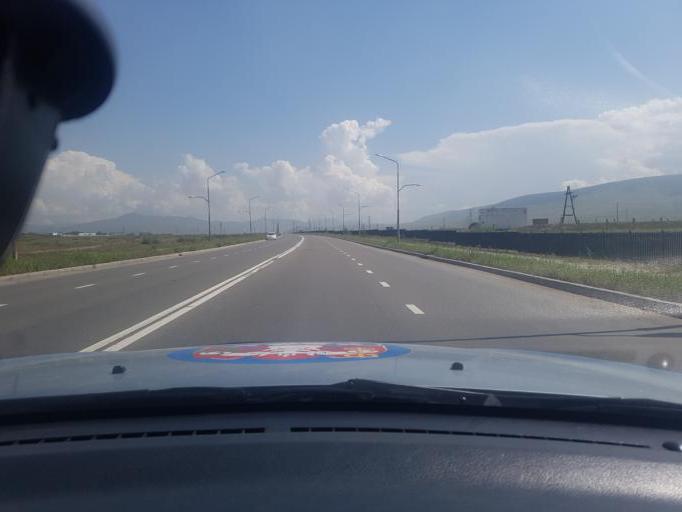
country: MN
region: Ulaanbaatar
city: Ulaanbaatar
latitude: 47.9016
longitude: 106.9861
